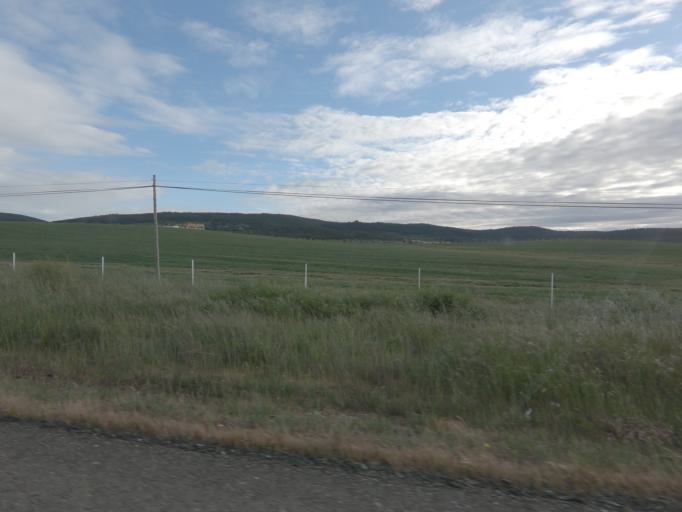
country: ES
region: Extremadura
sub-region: Provincia de Caceres
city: Pedroso de Acim
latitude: 39.8399
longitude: -6.3964
